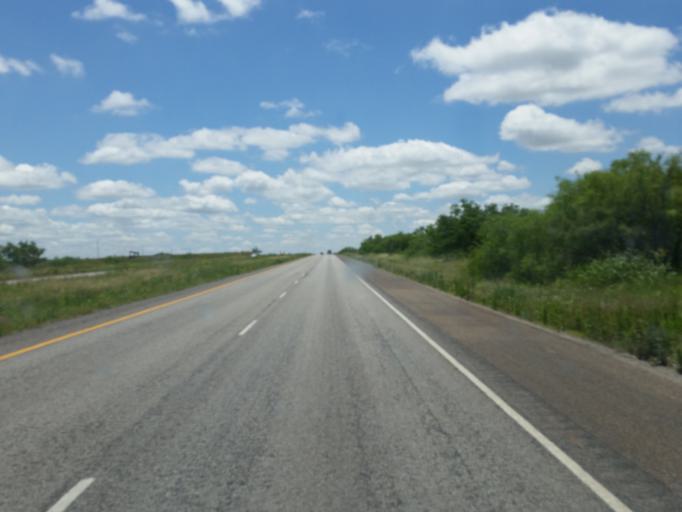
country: US
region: Texas
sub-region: Scurry County
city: Snyder
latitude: 32.9718
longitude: -101.0996
